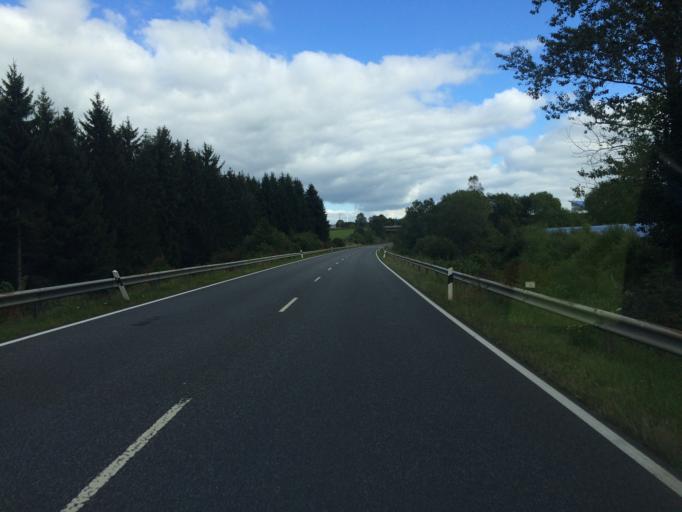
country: DE
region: Rheinland-Pfalz
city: Rennerod
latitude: 50.6201
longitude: 8.0666
